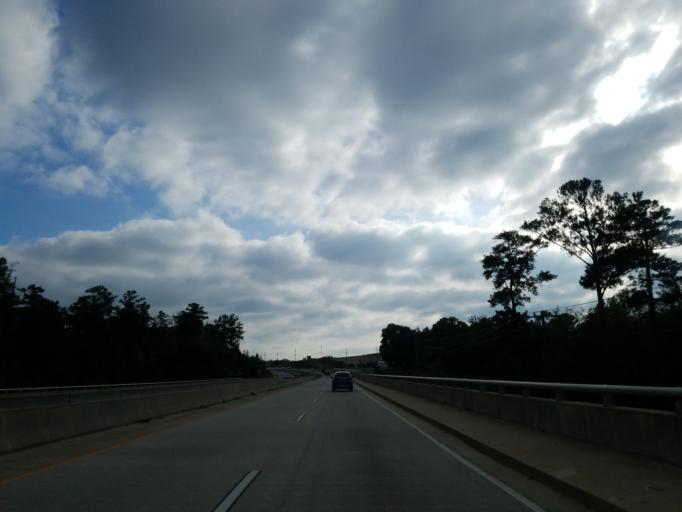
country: US
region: Georgia
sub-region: Cobb County
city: Acworth
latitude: 34.0900
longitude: -84.6531
